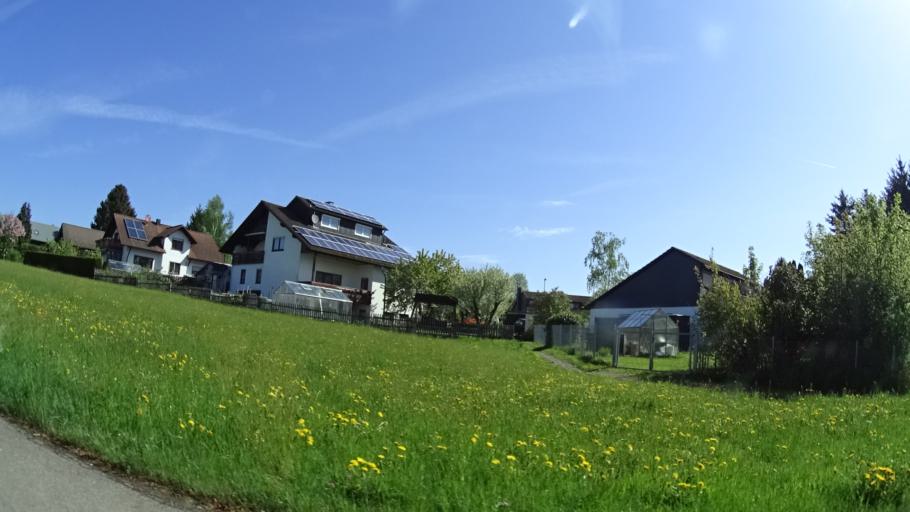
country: DE
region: Baden-Wuerttemberg
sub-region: Karlsruhe Region
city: Neuweiler
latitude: 48.6348
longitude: 8.5870
